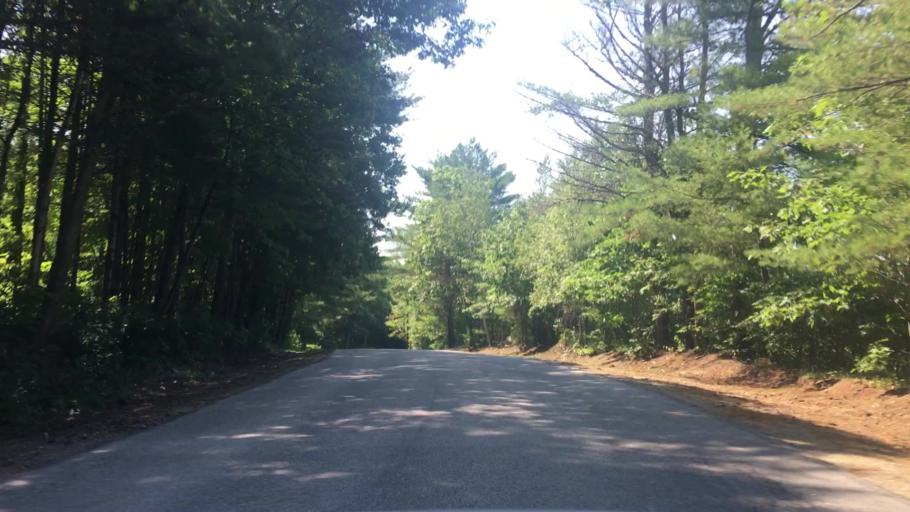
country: US
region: Maine
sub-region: Oxford County
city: South Paris
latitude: 44.2102
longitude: -70.5138
